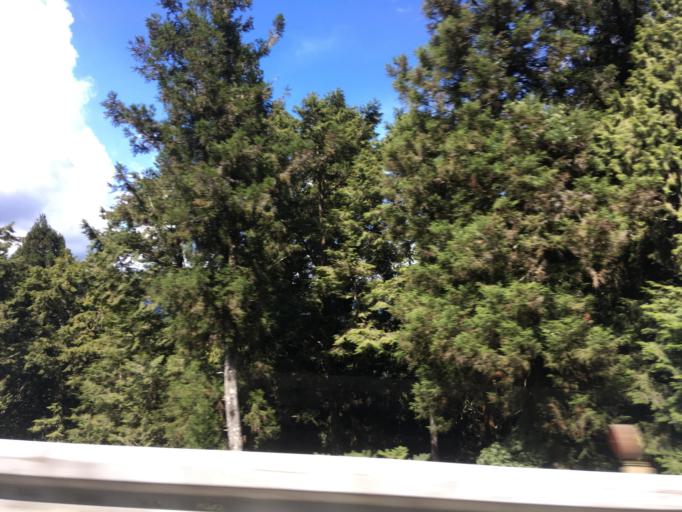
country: TW
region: Taiwan
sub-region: Yilan
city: Yilan
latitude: 24.5111
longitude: 121.5224
